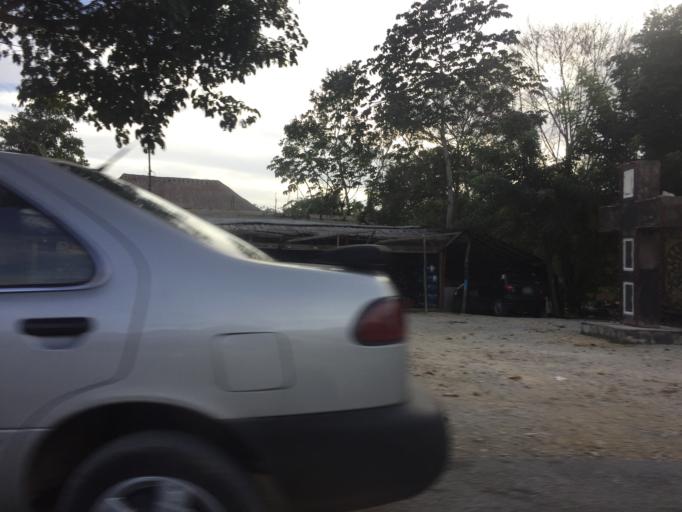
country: MX
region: Quintana Roo
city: Tulum
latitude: 20.3026
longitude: -87.5252
